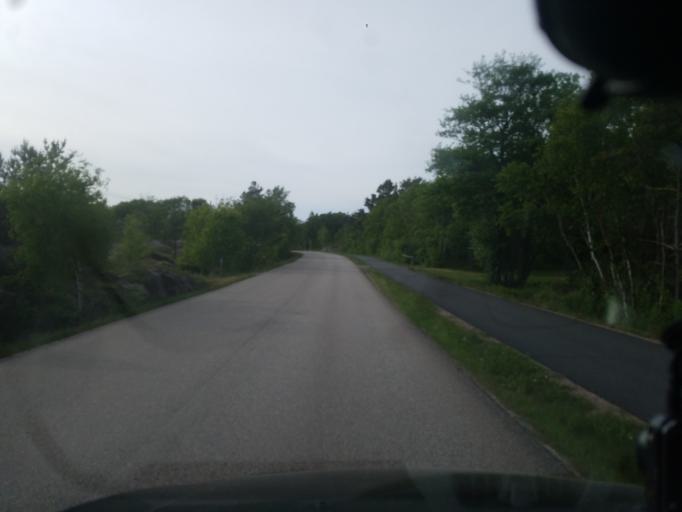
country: SE
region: Vaestra Goetaland
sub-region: Lysekils Kommun
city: Lysekil
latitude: 58.2921
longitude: 11.4556
